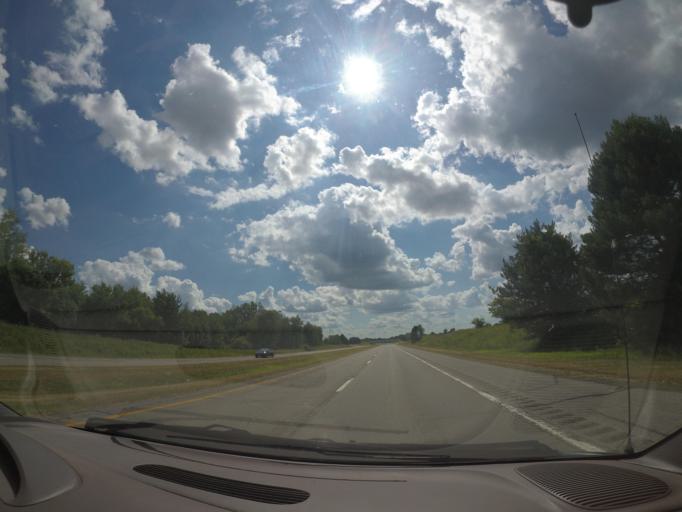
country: US
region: Ohio
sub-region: Huron County
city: Norwalk
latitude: 41.2244
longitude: -82.5917
